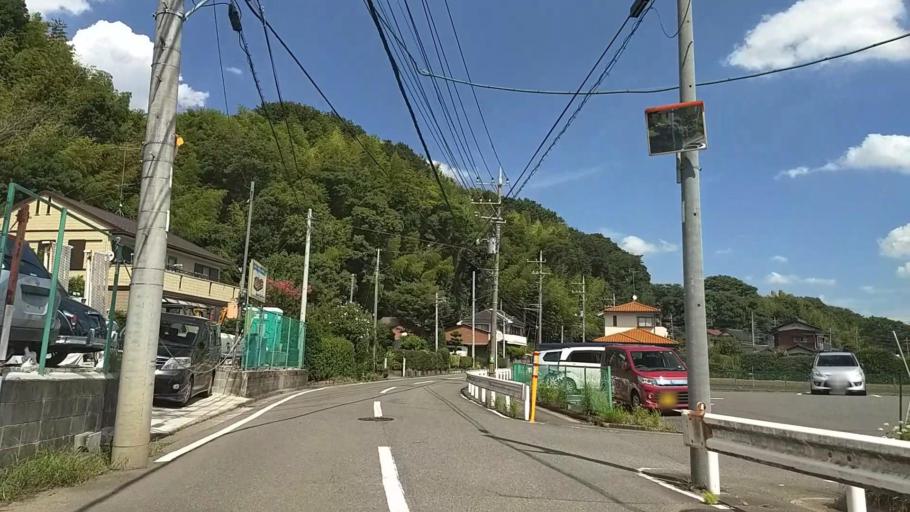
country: JP
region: Kanagawa
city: Yokohama
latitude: 35.5238
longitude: 139.5866
